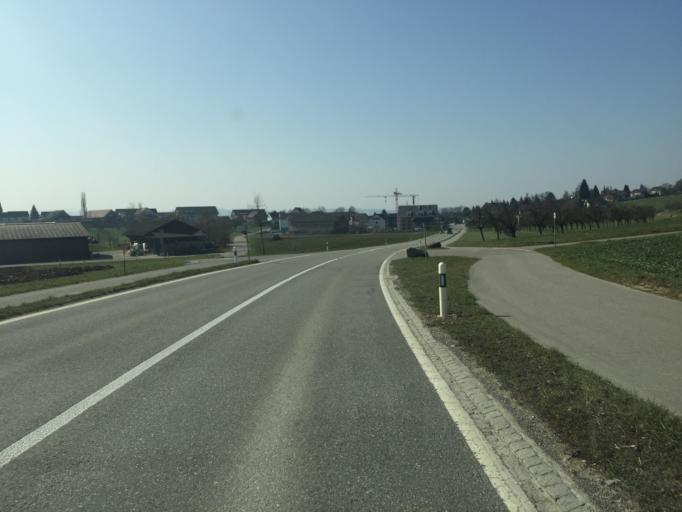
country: CH
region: Thurgau
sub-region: Frauenfeld District
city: Huttwilen
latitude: 47.5929
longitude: 8.8919
